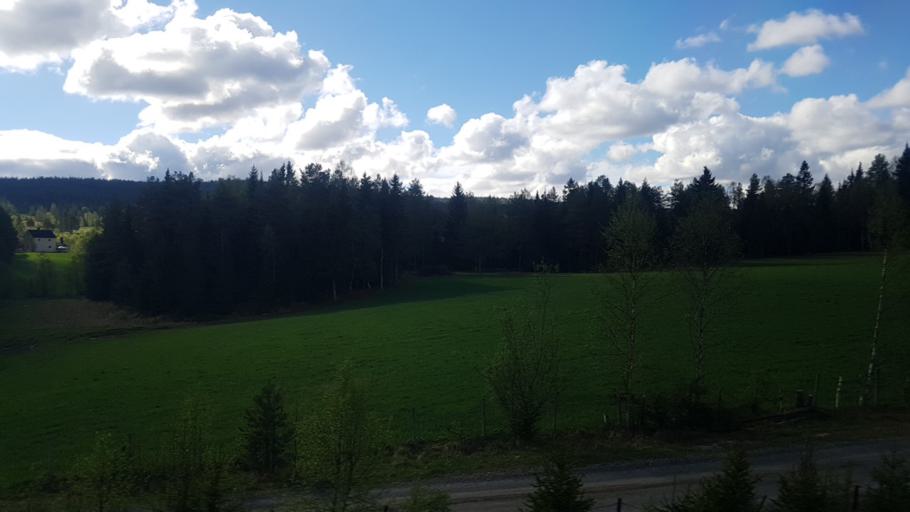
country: NO
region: Sor-Trondelag
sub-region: Rennebu
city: Berkak
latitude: 62.9224
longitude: 10.1549
